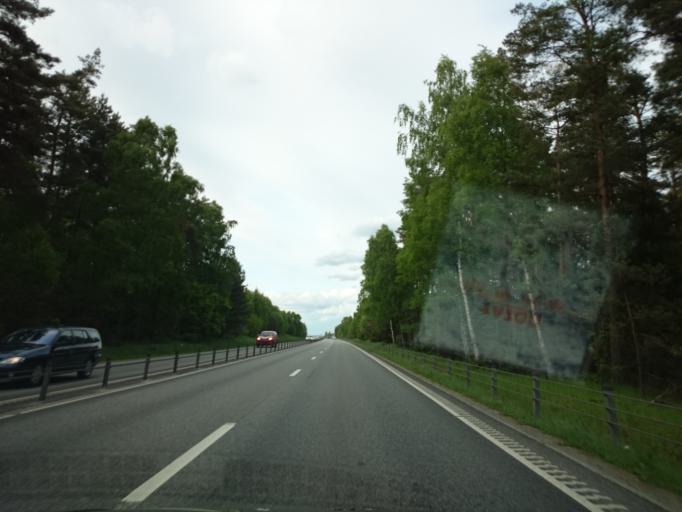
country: SE
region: Skane
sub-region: Kristianstads Kommun
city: Norra Asum
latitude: 55.9781
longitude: 14.0842
